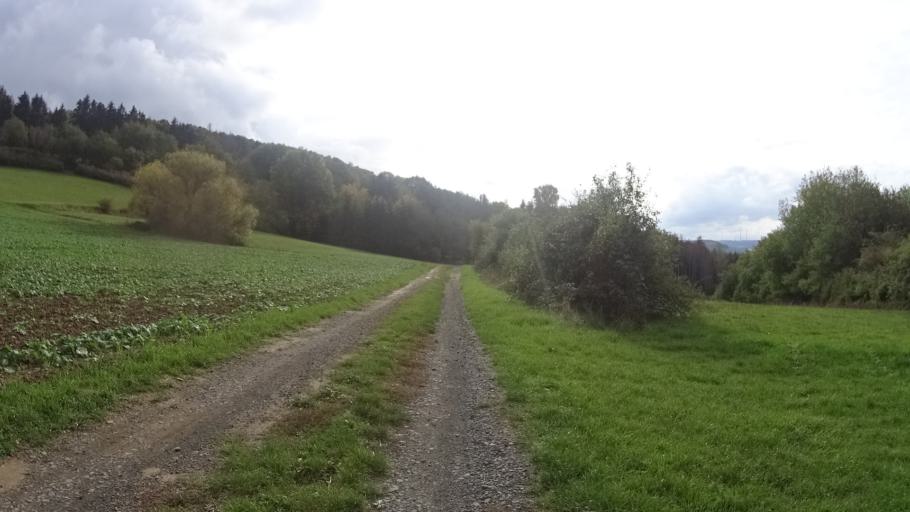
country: DE
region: Rheinland-Pfalz
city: Rockenhausen
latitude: 49.6394
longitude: 7.8441
